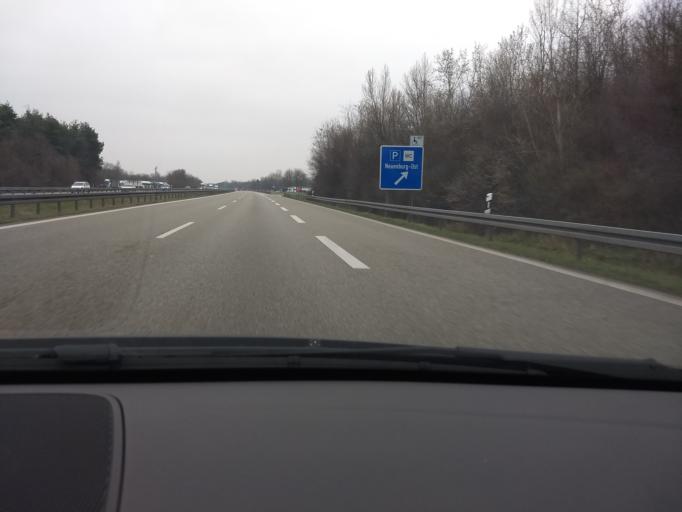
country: DE
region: Baden-Wuerttemberg
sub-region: Freiburg Region
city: Neuenburg am Rhein
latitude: 47.8272
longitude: 7.5619
